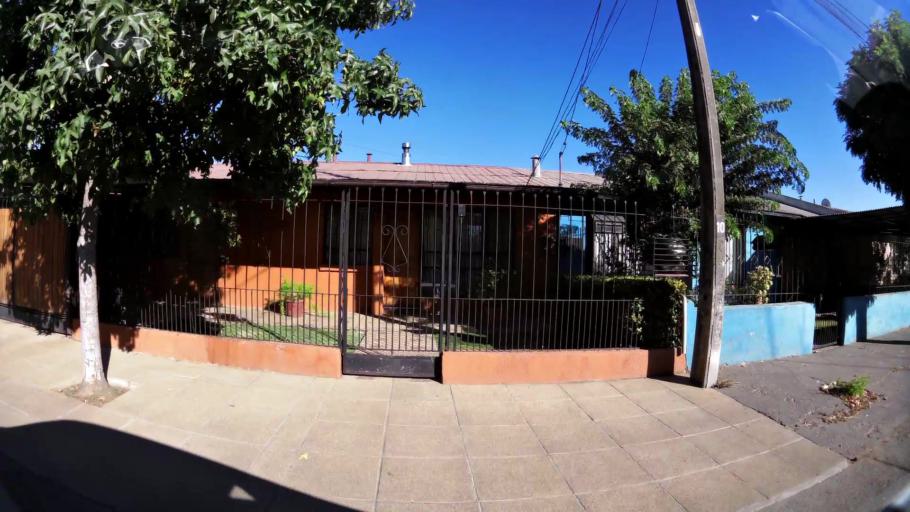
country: CL
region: O'Higgins
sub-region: Provincia de Cachapoal
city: Rancagua
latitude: -34.1807
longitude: -70.7253
